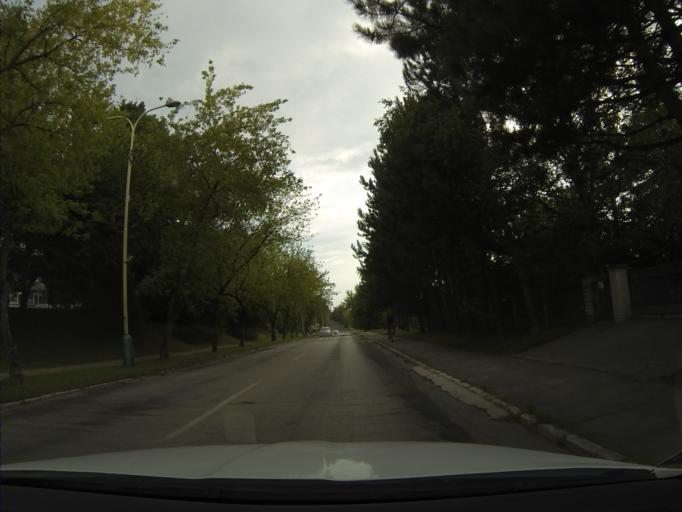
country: SK
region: Nitriansky
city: Prievidza
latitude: 48.7766
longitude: 18.6421
